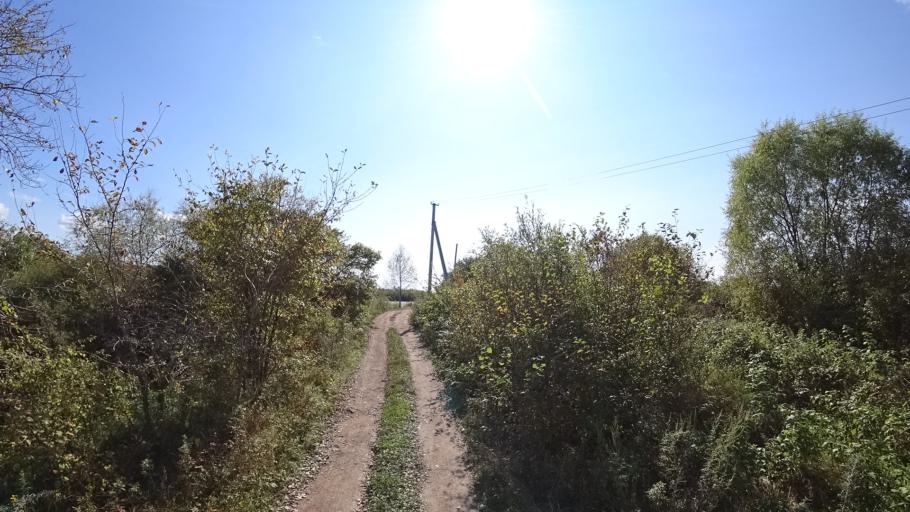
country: RU
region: Amur
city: Arkhara
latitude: 49.3992
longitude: 130.1305
